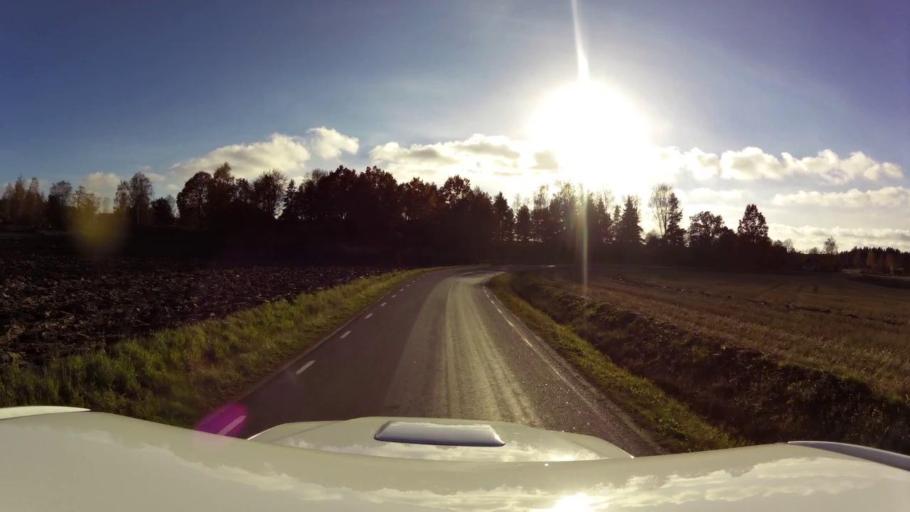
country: SE
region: OEstergoetland
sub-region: Linkopings Kommun
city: Vikingstad
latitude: 58.2848
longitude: 15.4397
